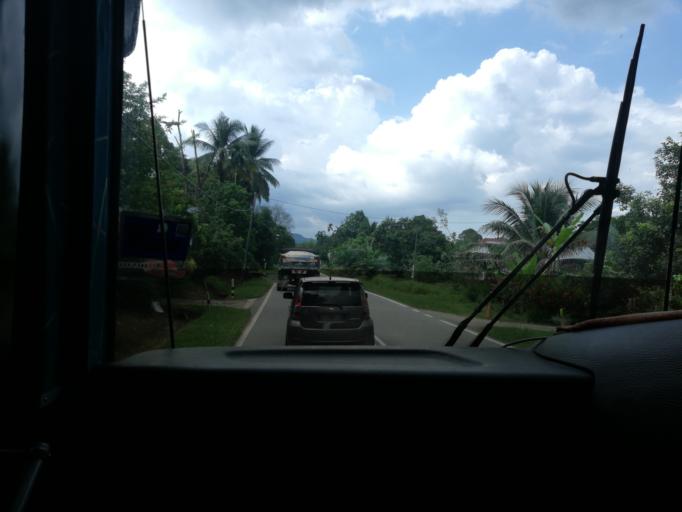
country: MY
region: Penang
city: Nibong Tebal
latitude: 5.2264
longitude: 100.6070
